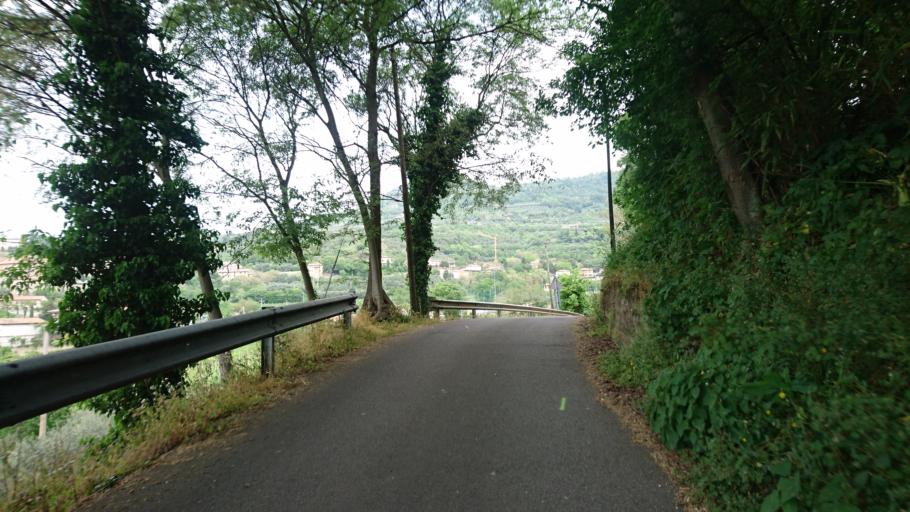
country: IT
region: Veneto
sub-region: Provincia di Padova
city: Arqua Petrarca
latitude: 45.2663
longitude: 11.7230
